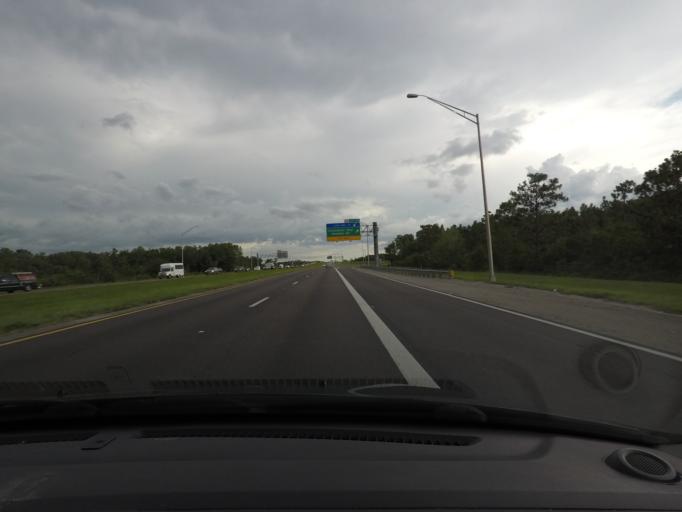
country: US
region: Florida
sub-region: Orange County
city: Conway
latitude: 28.4353
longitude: -81.2294
